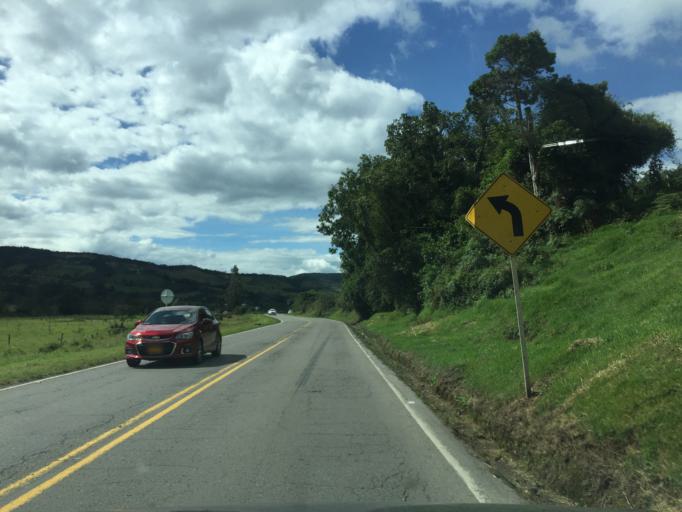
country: CO
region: Boyaca
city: Arcabuco
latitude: 5.7702
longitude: -73.4553
